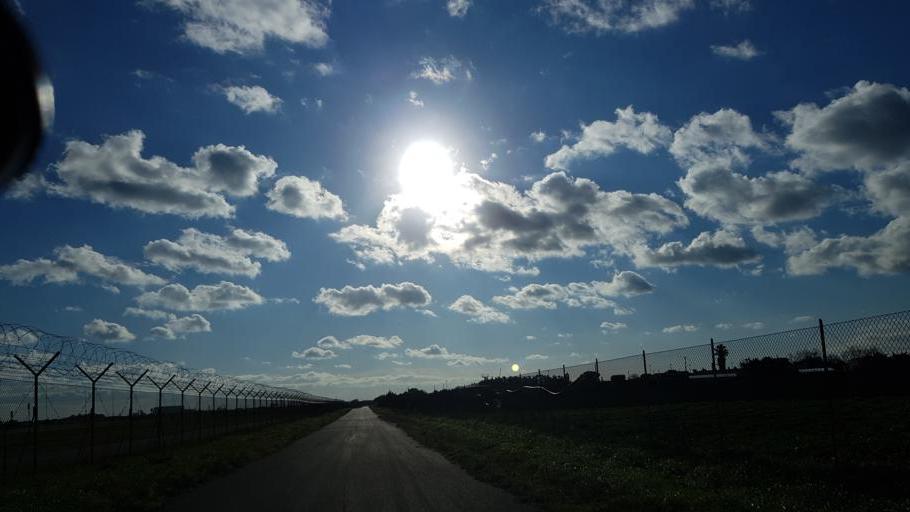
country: IT
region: Apulia
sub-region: Provincia di Brindisi
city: Materdomini
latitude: 40.6662
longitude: 17.9344
